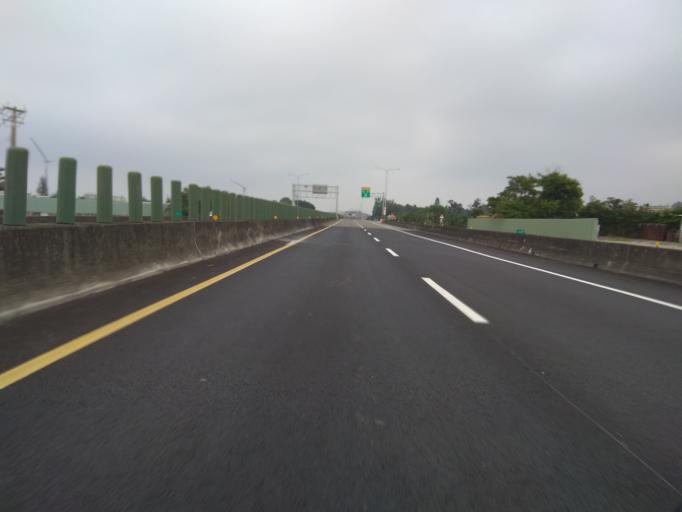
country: TW
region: Taiwan
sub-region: Hsinchu
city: Hsinchu
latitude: 24.7069
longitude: 120.8676
